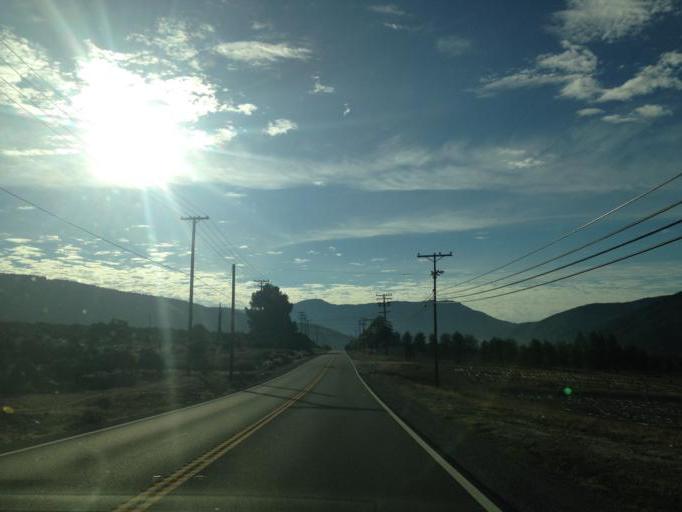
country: US
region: California
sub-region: San Diego County
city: Valley Center
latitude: 33.3108
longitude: -116.9859
